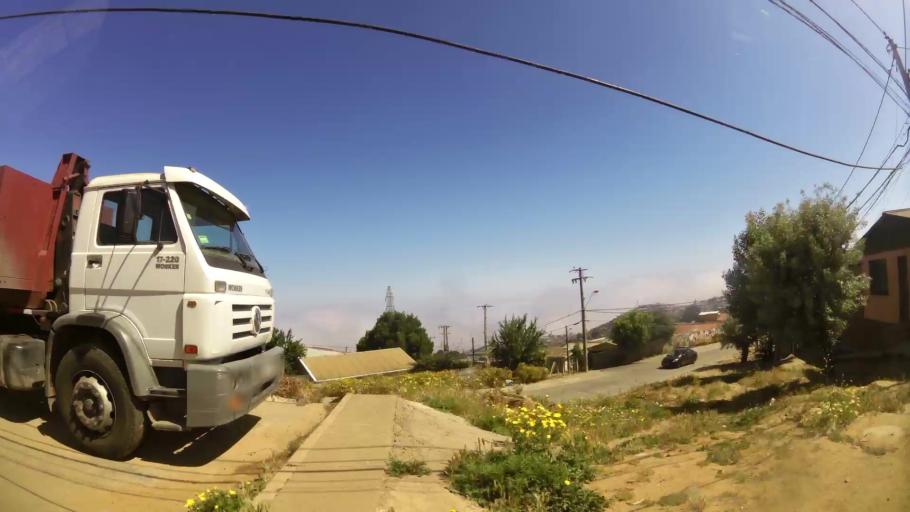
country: CL
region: Valparaiso
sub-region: Provincia de Valparaiso
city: Valparaiso
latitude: -33.0457
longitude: -71.6491
